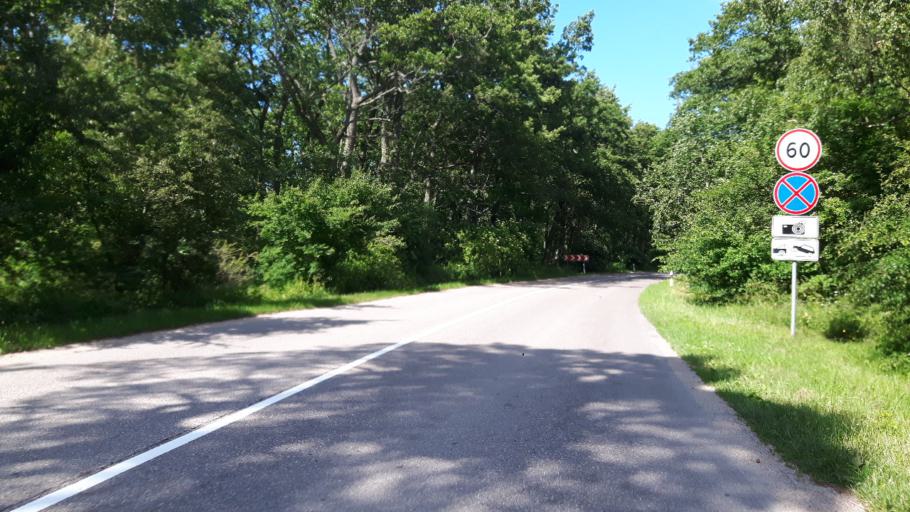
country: RU
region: Kaliningrad
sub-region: Zelenogradskiy Rayon
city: Zelenogradsk
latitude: 55.0216
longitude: 20.6207
